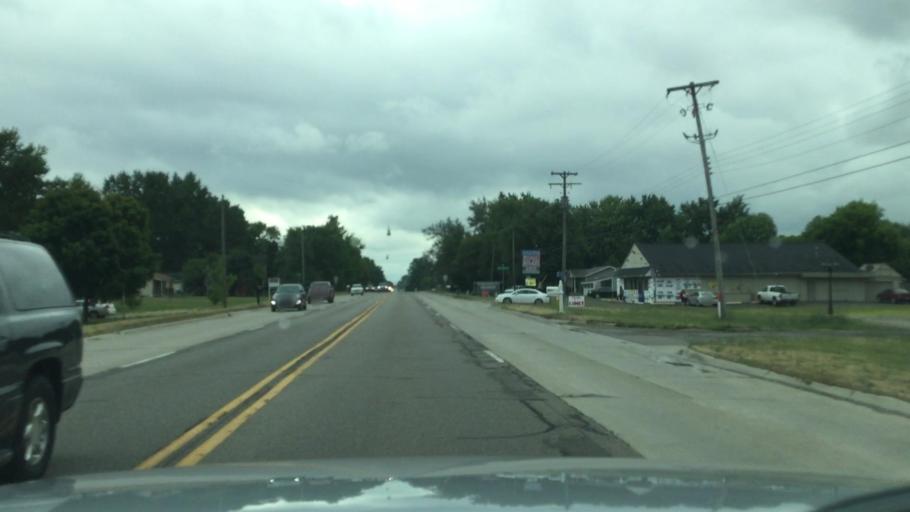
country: US
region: Michigan
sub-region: Genesee County
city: Burton
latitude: 43.0602
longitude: -83.6164
